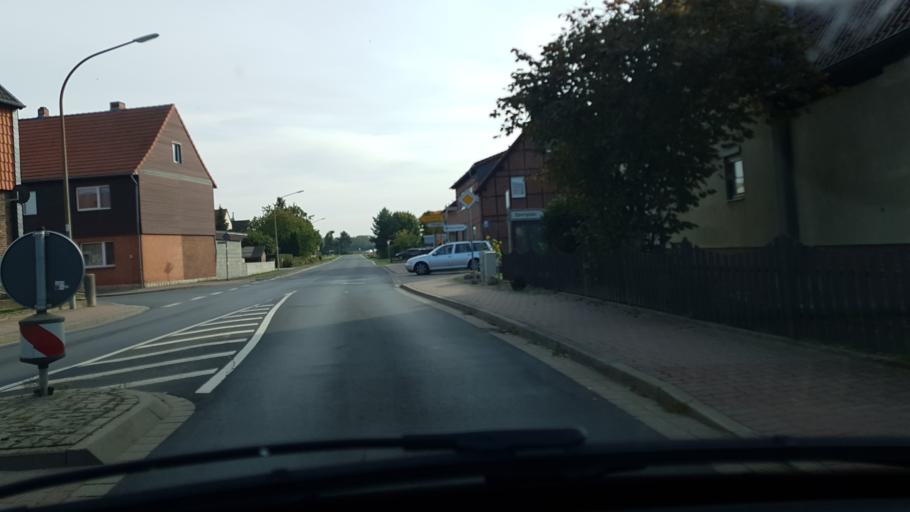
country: DE
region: Lower Saxony
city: Lehre
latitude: 52.3059
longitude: 10.6589
